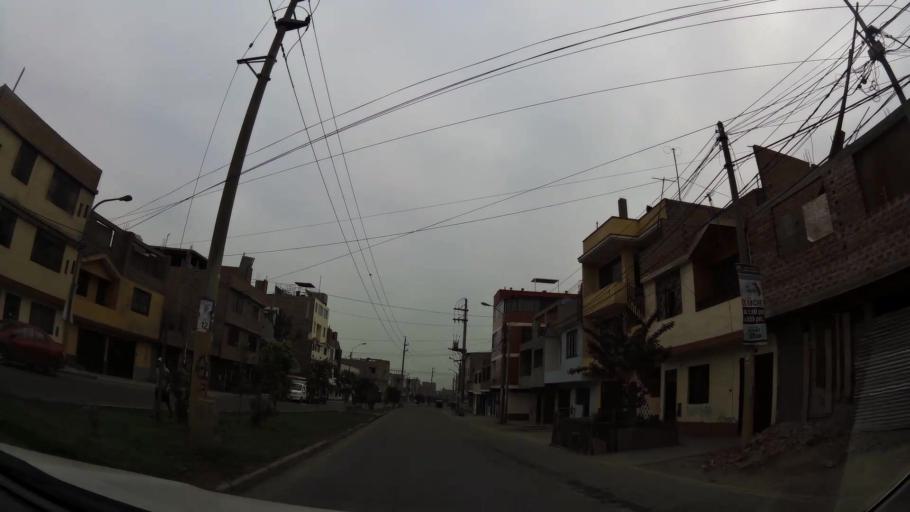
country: PE
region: Lima
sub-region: Lima
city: Independencia
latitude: -11.9606
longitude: -76.9917
